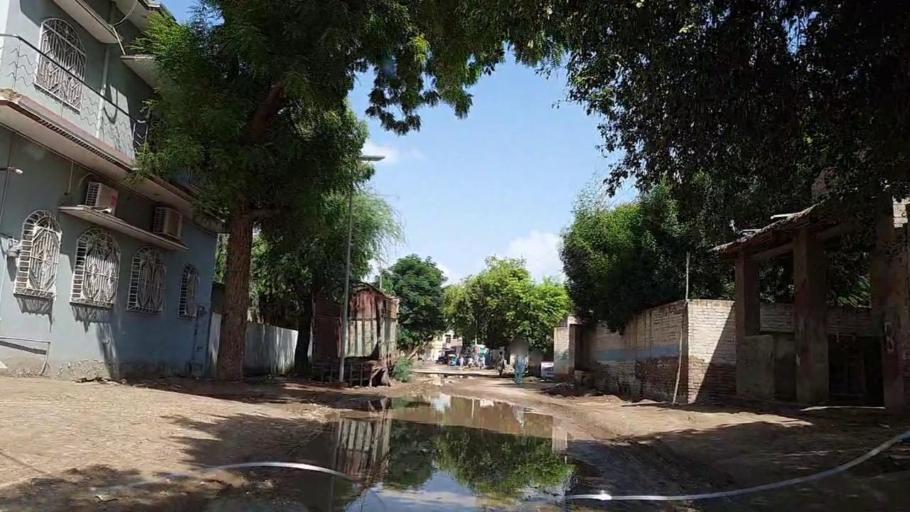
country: PK
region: Sindh
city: Pad Idan
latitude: 26.7753
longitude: 68.2978
